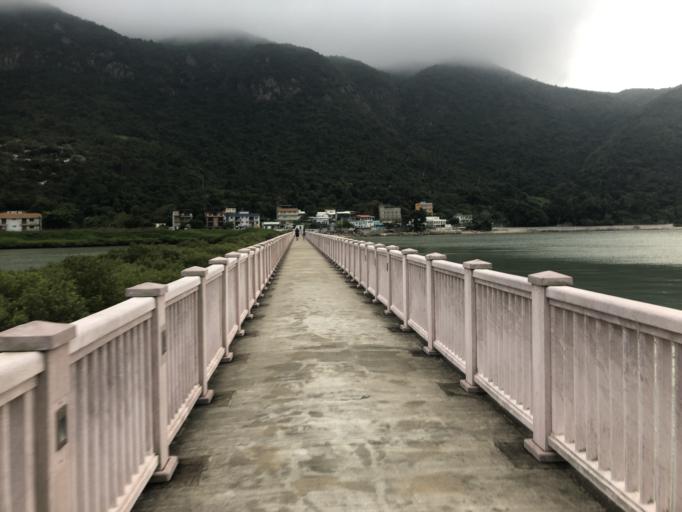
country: HK
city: Tai O
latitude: 22.2492
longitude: 113.8610
